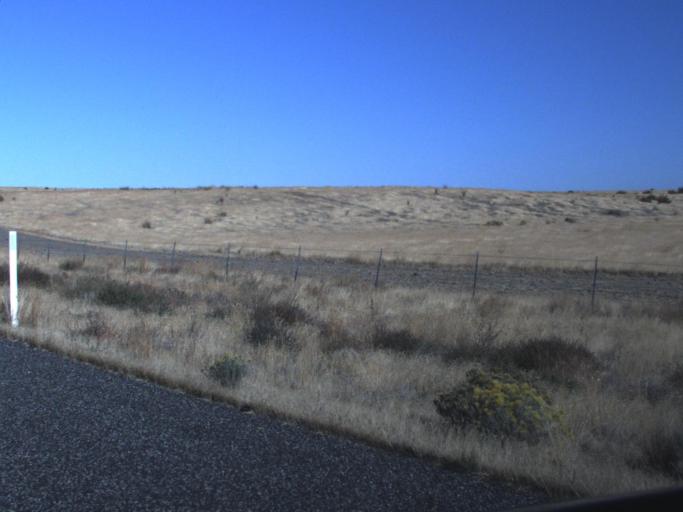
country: US
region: Washington
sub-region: Benton County
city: West Richland
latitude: 46.4111
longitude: -119.4536
